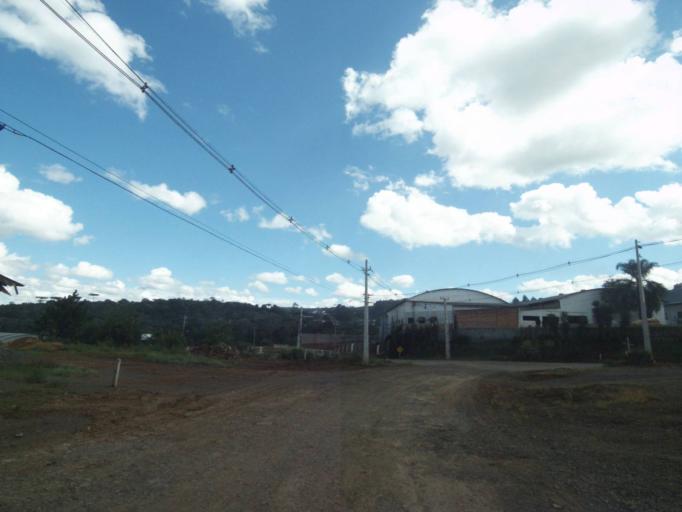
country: BR
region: Parana
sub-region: Uniao Da Vitoria
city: Uniao da Vitoria
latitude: -26.1530
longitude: -51.5384
